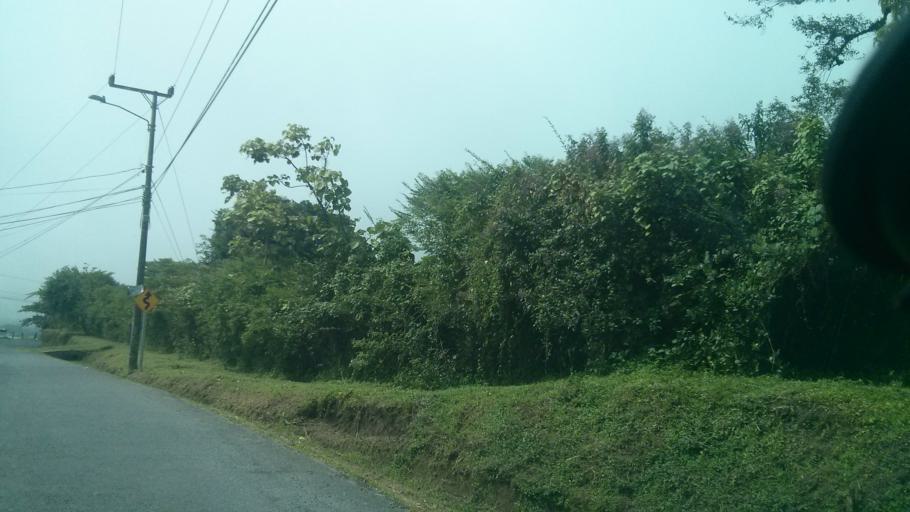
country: CR
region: San Jose
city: Ipis
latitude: 9.9974
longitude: -83.9601
